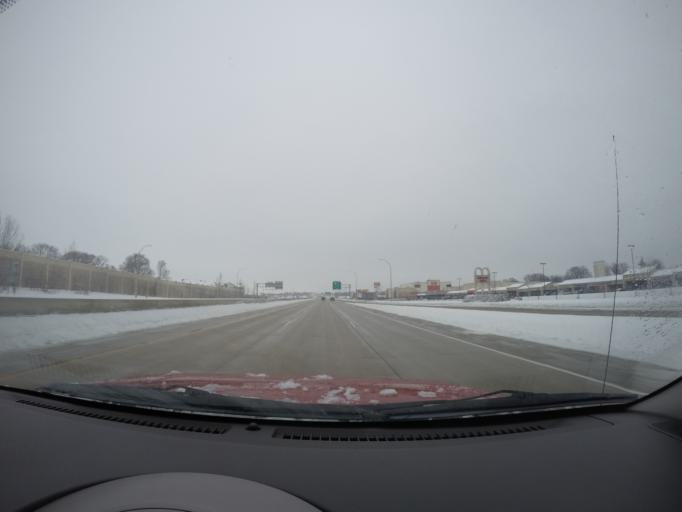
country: US
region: Minnesota
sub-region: Olmsted County
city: Rochester
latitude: 44.0275
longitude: -92.4879
